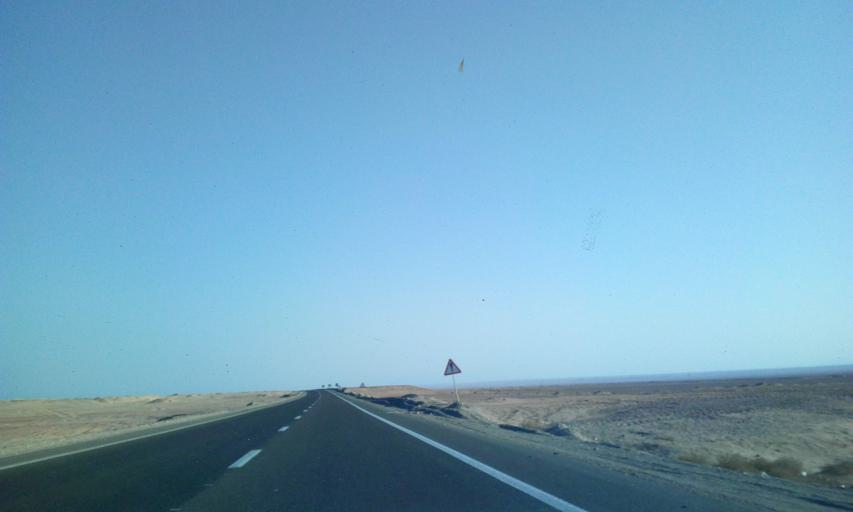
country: EG
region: South Sinai
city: Tor
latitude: 28.6713
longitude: 32.8359
